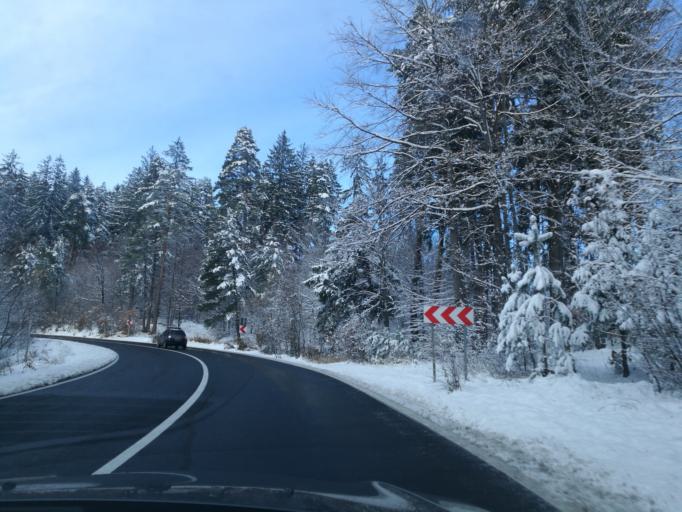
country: RO
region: Brasov
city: Brasov
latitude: 45.6283
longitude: 25.5568
